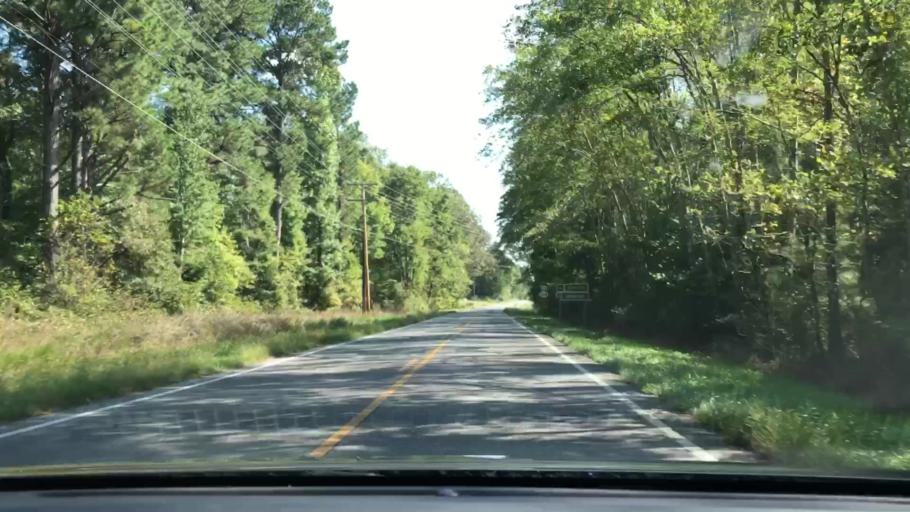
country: US
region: Kentucky
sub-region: Marshall County
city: Benton
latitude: 36.7648
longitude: -88.2475
